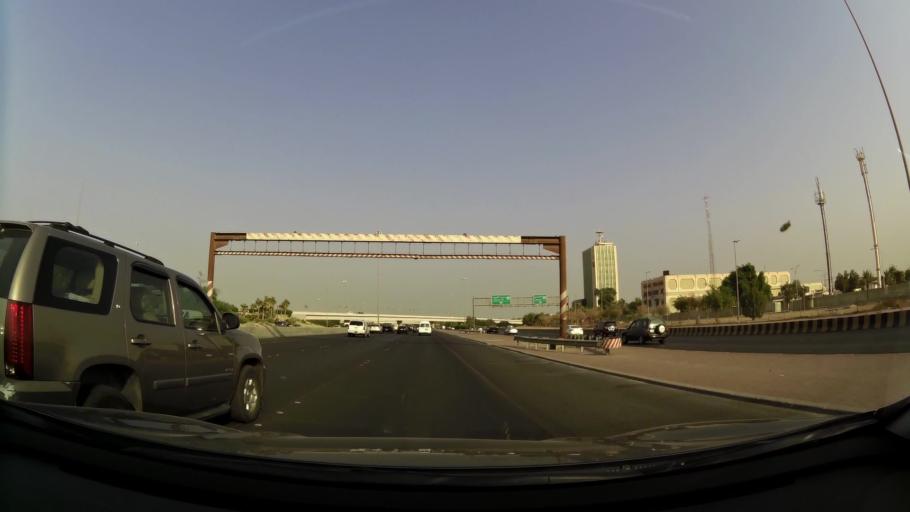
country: KW
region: Muhafazat Hawalli
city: Hawalli
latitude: 29.3068
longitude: 48.0173
